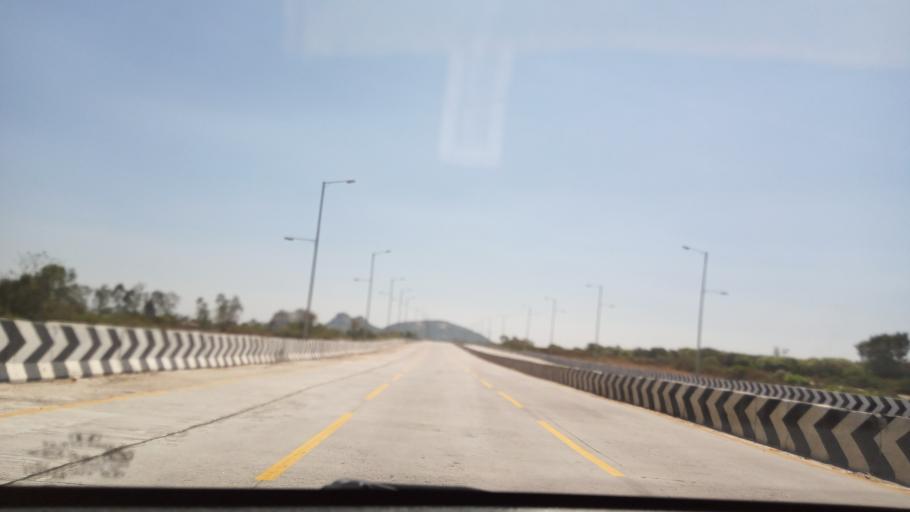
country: IN
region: Andhra Pradesh
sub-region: Chittoor
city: Palmaner
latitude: 13.1849
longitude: 78.6074
